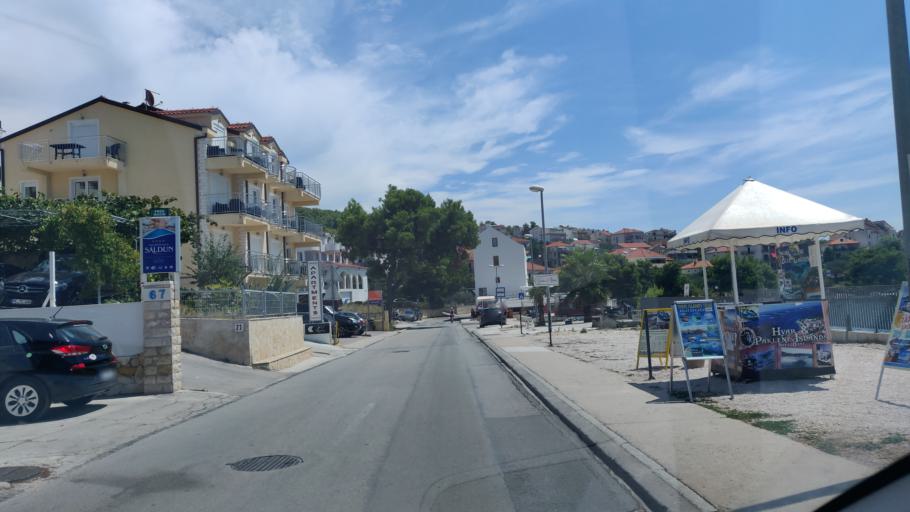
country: HR
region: Splitsko-Dalmatinska
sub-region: Grad Trogir
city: Trogir
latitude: 43.5079
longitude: 16.2579
